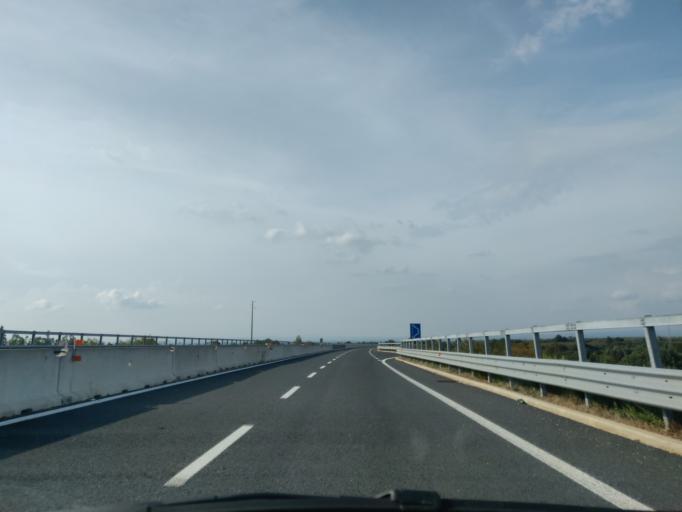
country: IT
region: Latium
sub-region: Provincia di Viterbo
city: Blera
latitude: 42.3273
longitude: 11.9868
